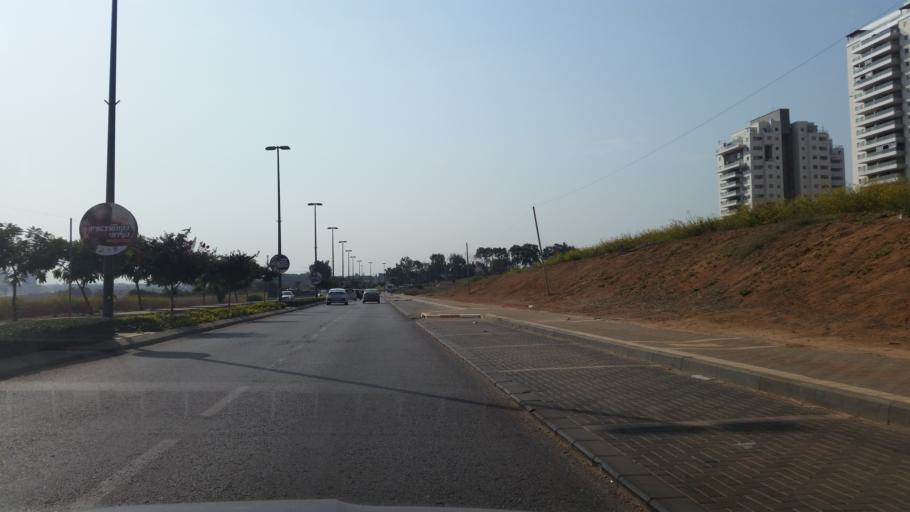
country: IL
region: Central District
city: Netanya
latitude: 32.3112
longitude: 34.8613
